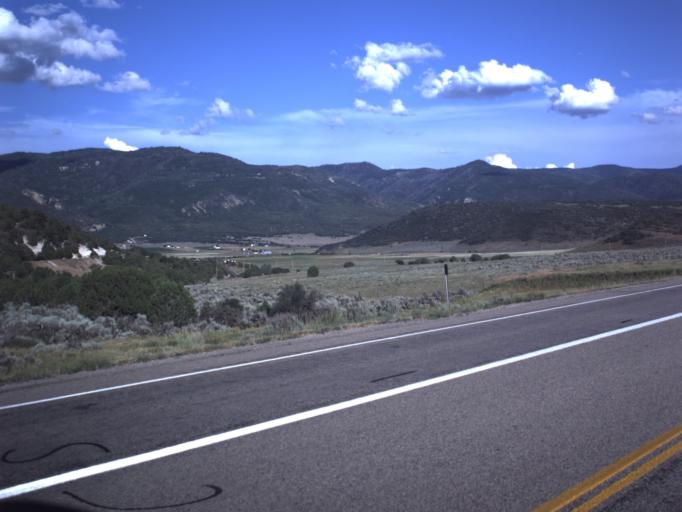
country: US
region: Utah
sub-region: Sanpete County
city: Fairview
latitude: 39.7069
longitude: -111.4699
